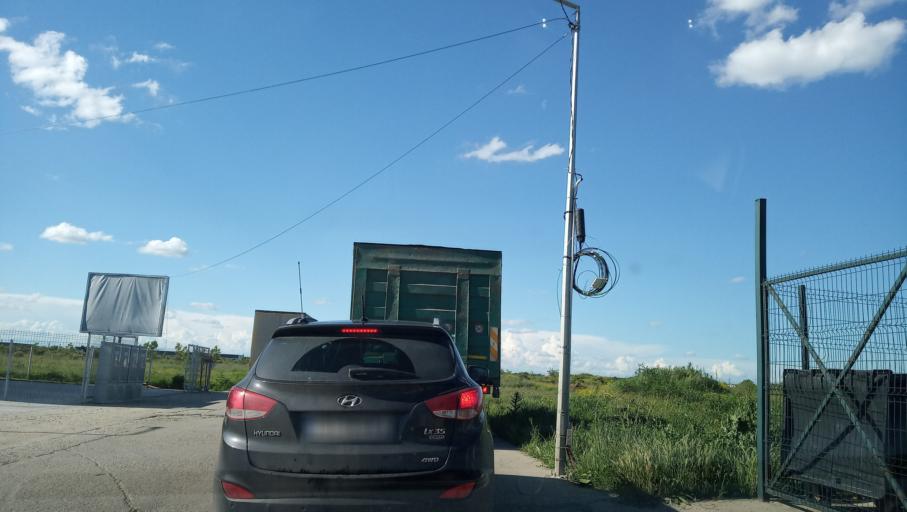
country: RO
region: Ilfov
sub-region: Comuna Chiajna
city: Chiajna
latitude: 44.4469
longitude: 25.9580
